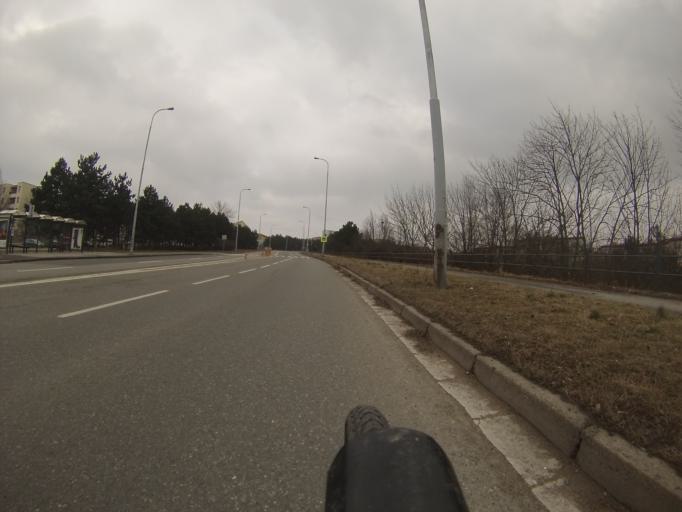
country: CZ
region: South Moravian
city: Bilovice nad Svitavou
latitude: 49.2040
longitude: 16.6791
